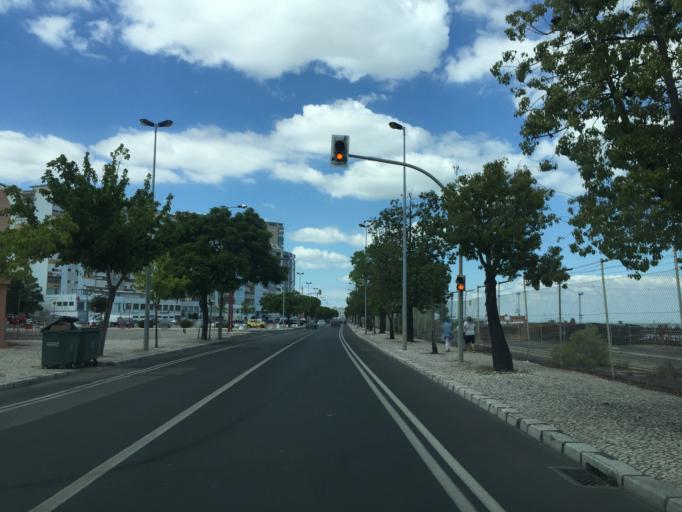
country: PT
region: Setubal
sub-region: Almada
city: Cacilhas
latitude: 38.6817
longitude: -9.1487
